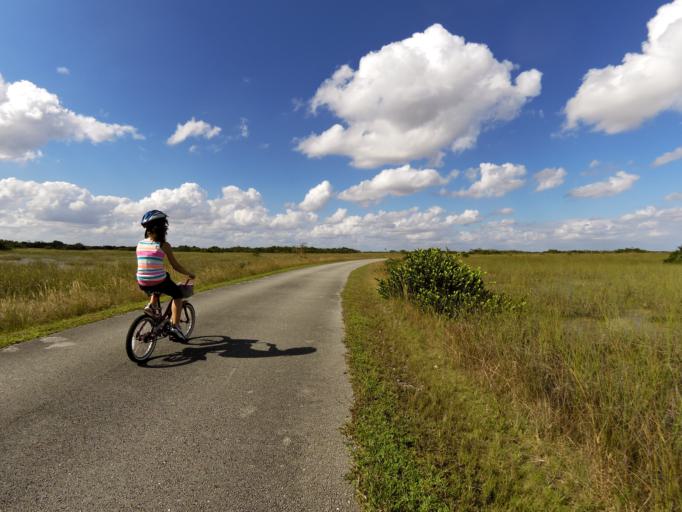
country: US
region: Florida
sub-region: Miami-Dade County
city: The Hammocks
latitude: 25.7063
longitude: -80.7617
